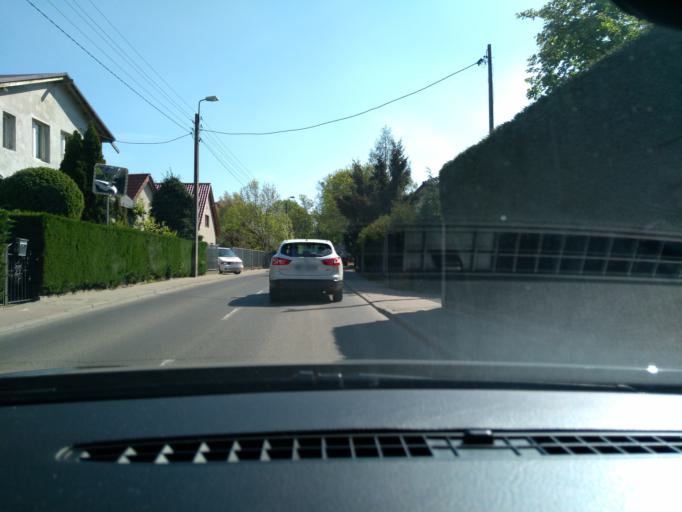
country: PL
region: West Pomeranian Voivodeship
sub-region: Szczecin
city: Szczecin
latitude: 53.4787
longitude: 14.5122
